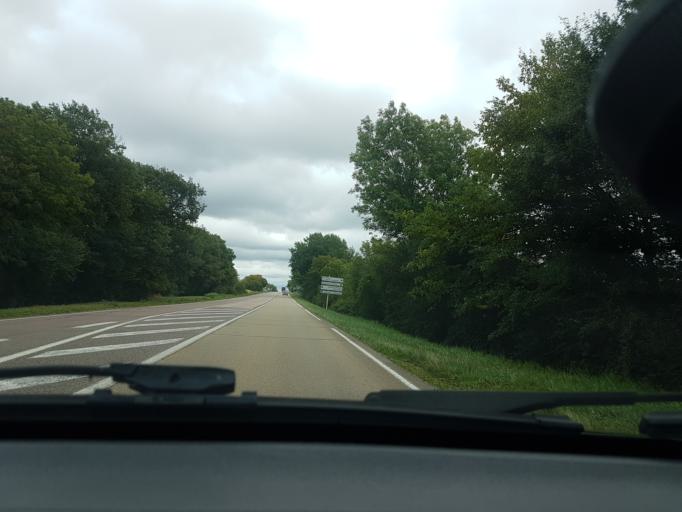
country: FR
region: Bourgogne
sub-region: Departement de la Cote-d'Or
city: Saulieu
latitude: 47.4270
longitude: 4.1085
